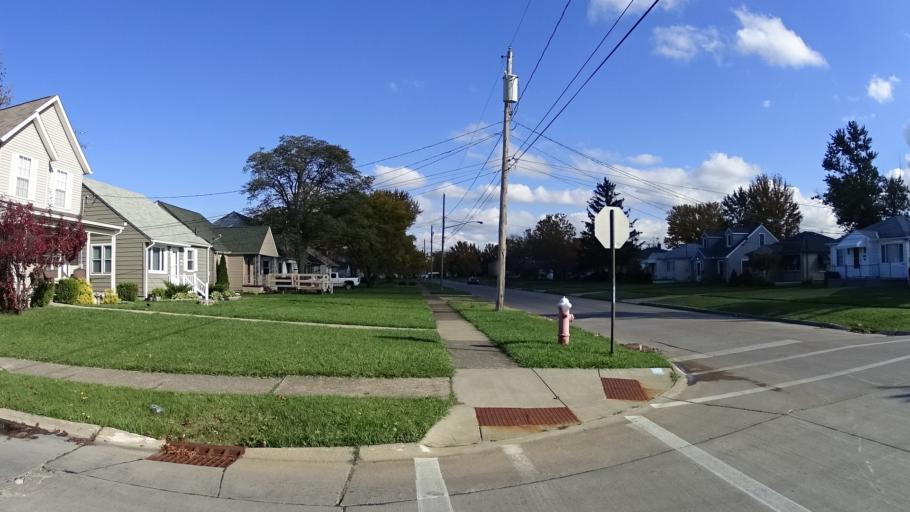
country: US
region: Ohio
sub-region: Lorain County
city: Lorain
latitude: 41.4492
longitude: -82.1887
